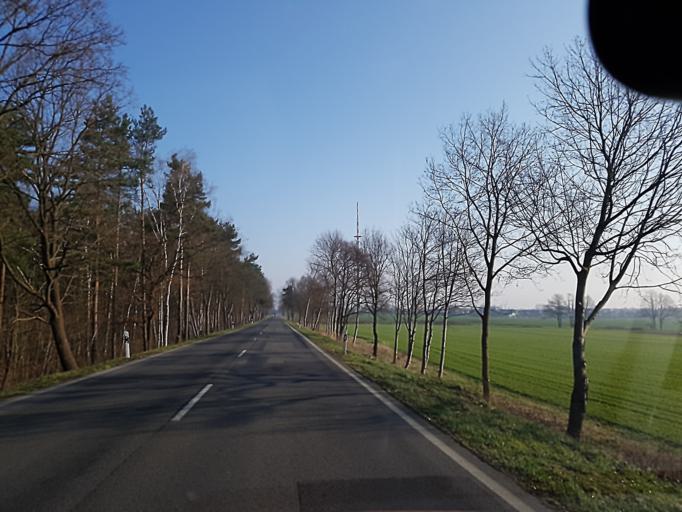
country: DE
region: Brandenburg
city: Calau
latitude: 51.7347
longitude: 13.9365
